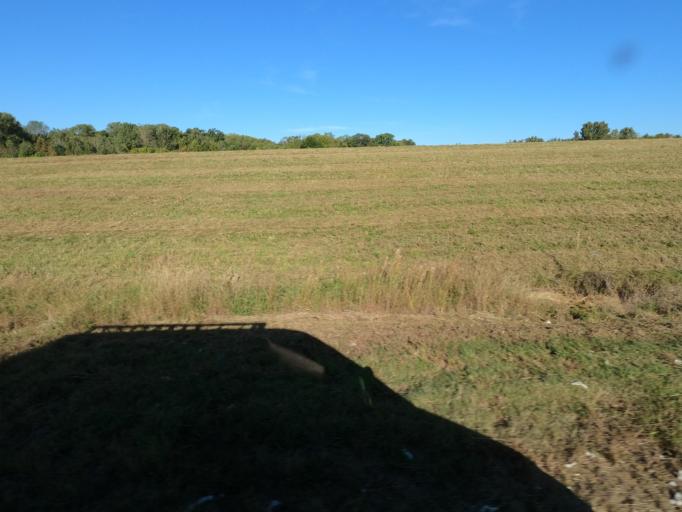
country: US
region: Tennessee
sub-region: Tipton County
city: Munford
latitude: 35.4197
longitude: -89.8208
